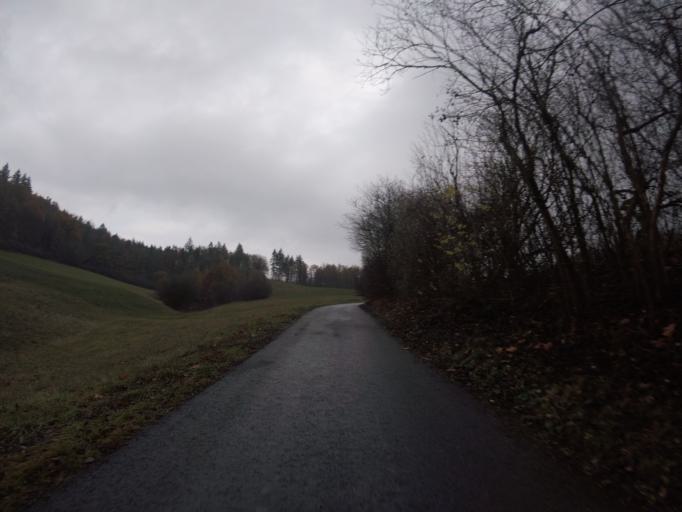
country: DE
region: Baden-Wuerttemberg
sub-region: Regierungsbezirk Stuttgart
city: Oppenweiler
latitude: 48.9817
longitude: 9.4365
